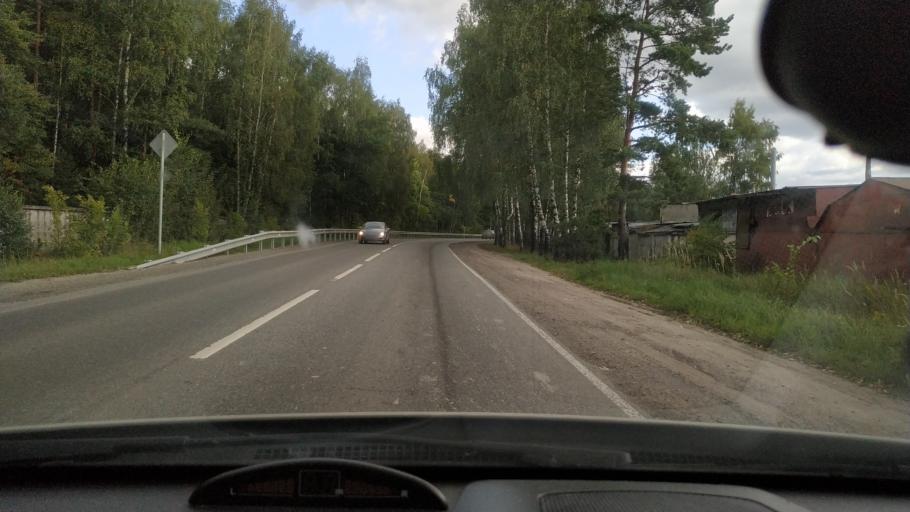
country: RU
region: Moskovskaya
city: Chornaya
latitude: 55.7650
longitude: 38.0702
